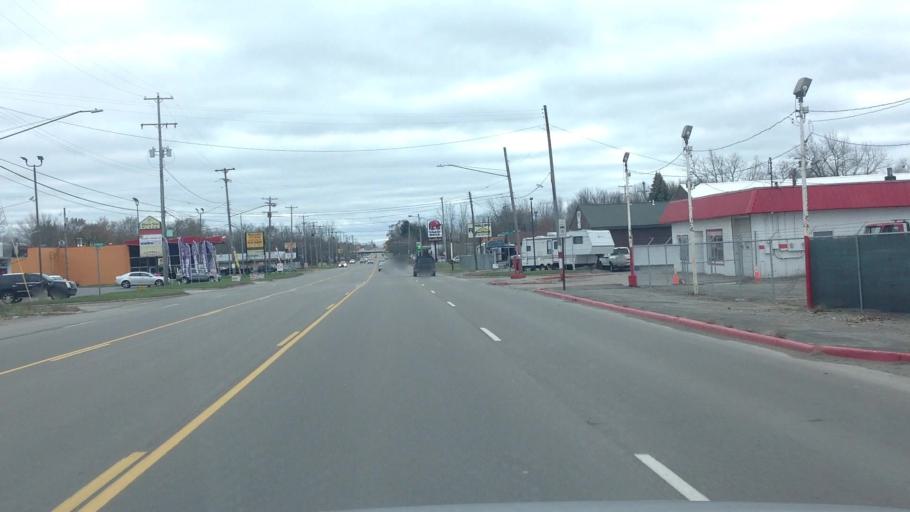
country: US
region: Michigan
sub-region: Genesee County
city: Mount Morris
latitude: 43.1086
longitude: -83.6944
